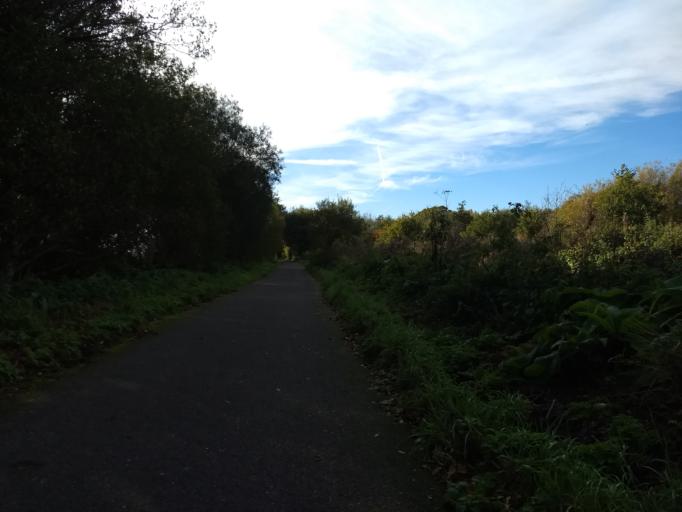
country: GB
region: England
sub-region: Isle of Wight
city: Newchurch
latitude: 50.6629
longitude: -1.2369
